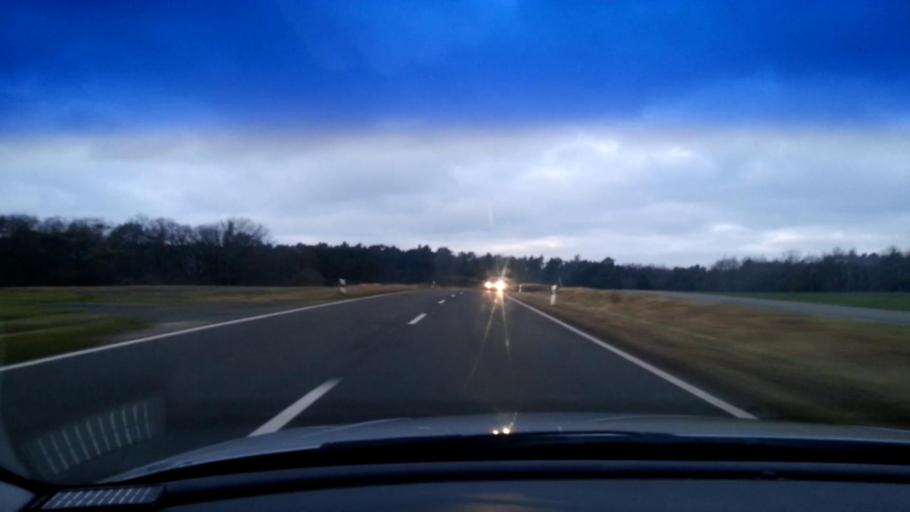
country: DE
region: Bavaria
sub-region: Upper Franconia
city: Frensdorf
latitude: 49.8357
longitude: 10.8732
